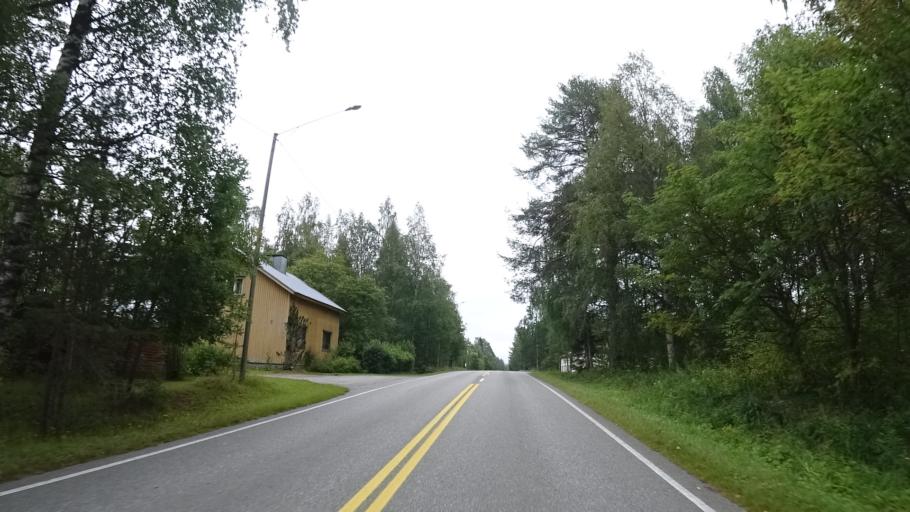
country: FI
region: North Karelia
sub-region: Pielisen Karjala
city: Lieksa
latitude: 63.2842
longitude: 30.5300
